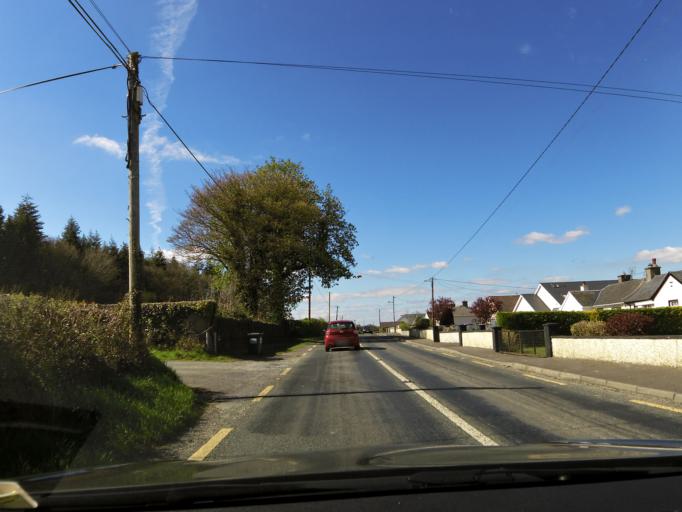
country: IE
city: Ballylinan
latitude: 53.0054
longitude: -7.0767
